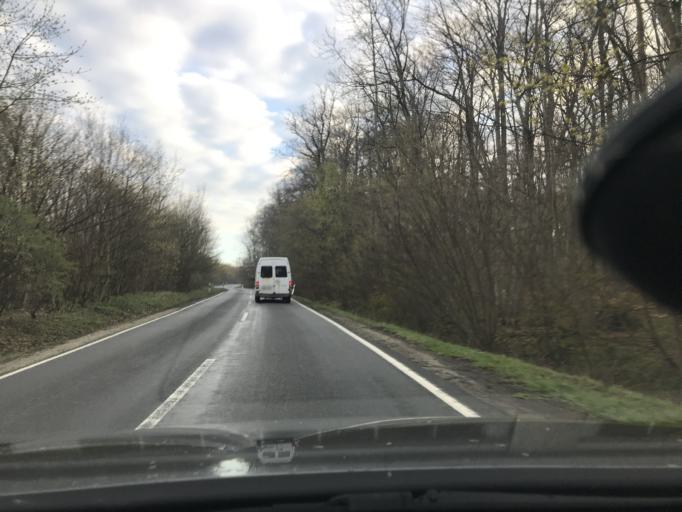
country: DE
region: Thuringia
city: Menteroda
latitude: 51.2949
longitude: 10.5528
